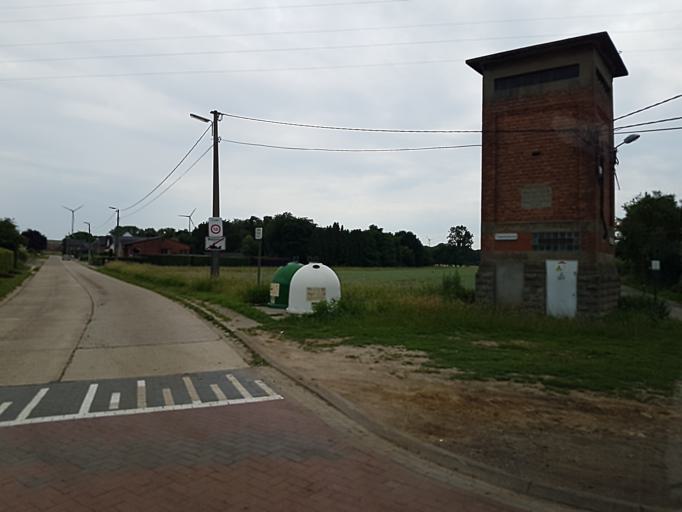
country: BE
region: Flanders
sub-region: Provincie Vlaams-Brabant
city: Diest
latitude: 50.9680
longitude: 5.0603
